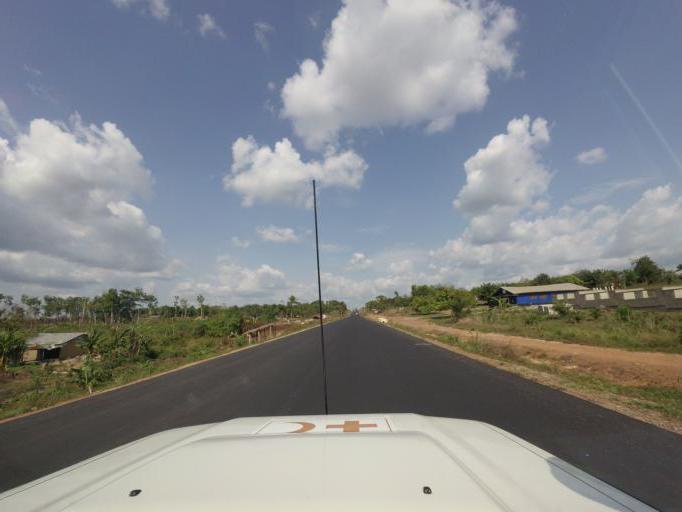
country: LR
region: Bong
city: Gbarnga
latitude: 6.9882
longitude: -9.5889
